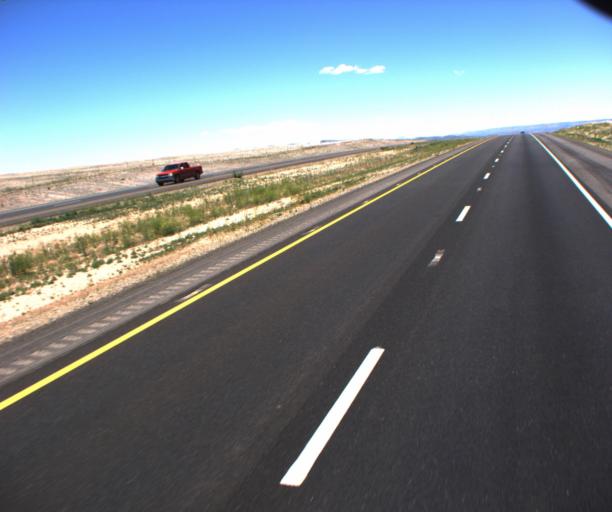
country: US
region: Arizona
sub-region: Yavapai County
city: Chino Valley
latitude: 34.6935
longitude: -112.4469
